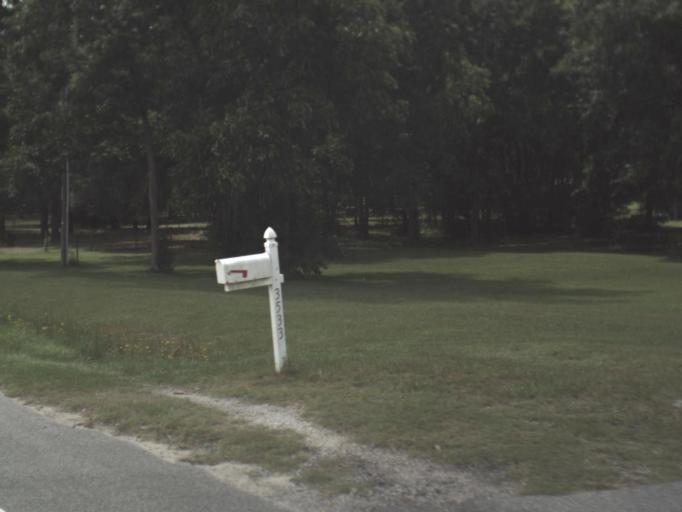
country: US
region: Florida
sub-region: Madison County
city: Madison
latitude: 30.4723
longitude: -83.3218
